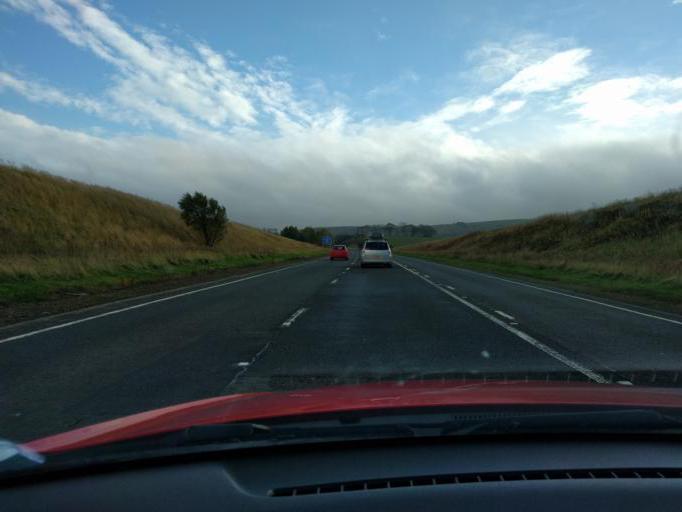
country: GB
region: Scotland
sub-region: The Scottish Borders
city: Duns
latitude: 55.9295
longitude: -2.3548
